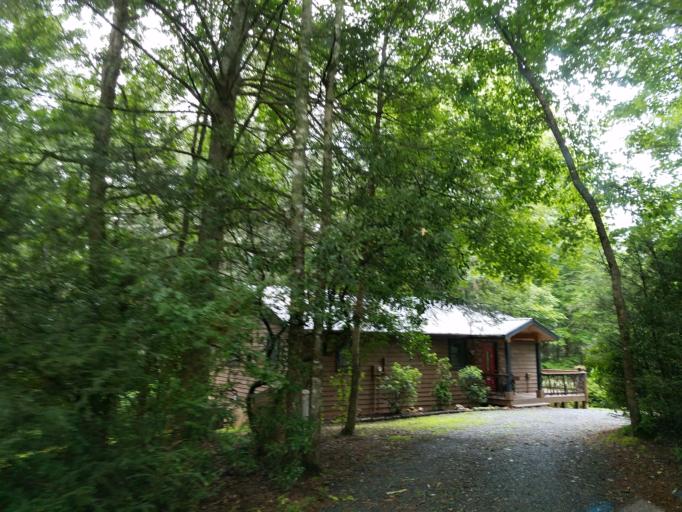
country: US
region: Georgia
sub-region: Fannin County
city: Blue Ridge
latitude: 34.7973
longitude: -84.2849
